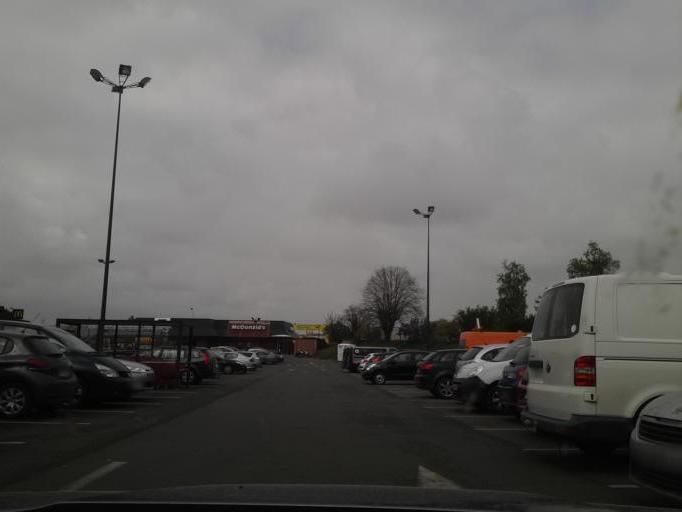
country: FR
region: Pays de la Loire
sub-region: Departement de la Vendee
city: Fontenay-le-Comte
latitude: 46.4522
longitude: -0.8044
